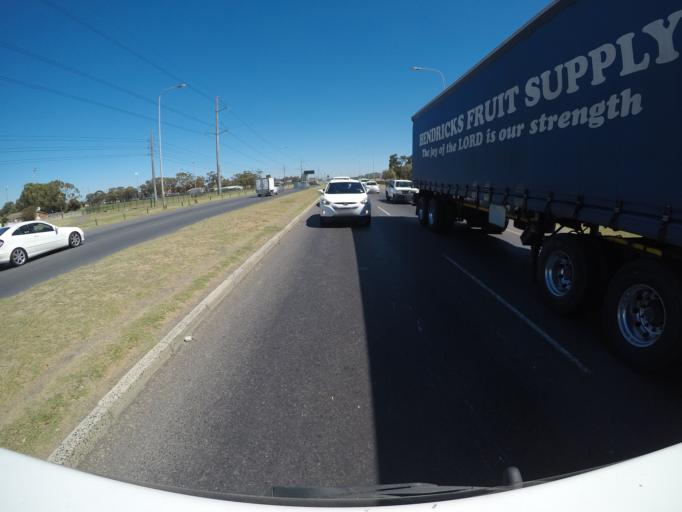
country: ZA
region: Western Cape
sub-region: Cape Winelands District Municipality
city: Stellenbosch
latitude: -34.0880
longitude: 18.8381
